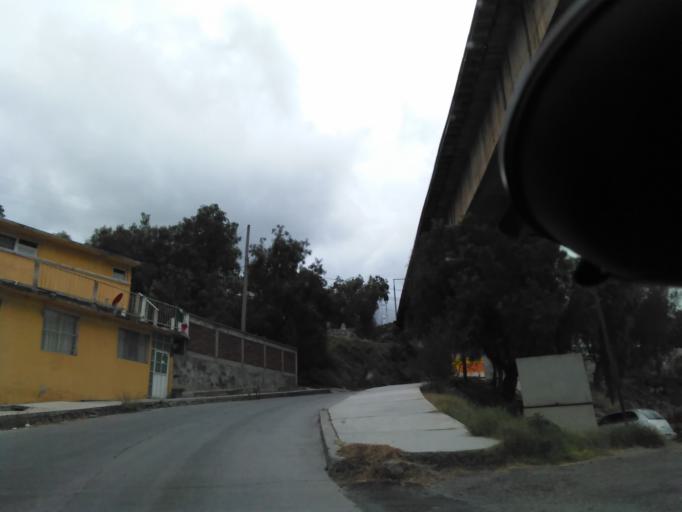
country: MX
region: Hidalgo
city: Tula de Allende
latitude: 20.0602
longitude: -99.3477
